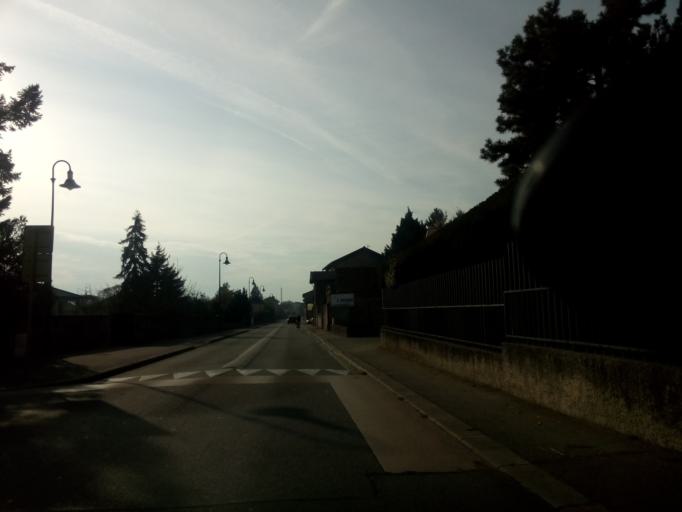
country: FR
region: Rhone-Alpes
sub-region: Departement du Rhone
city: Condrieu
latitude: 45.4671
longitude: 4.7727
